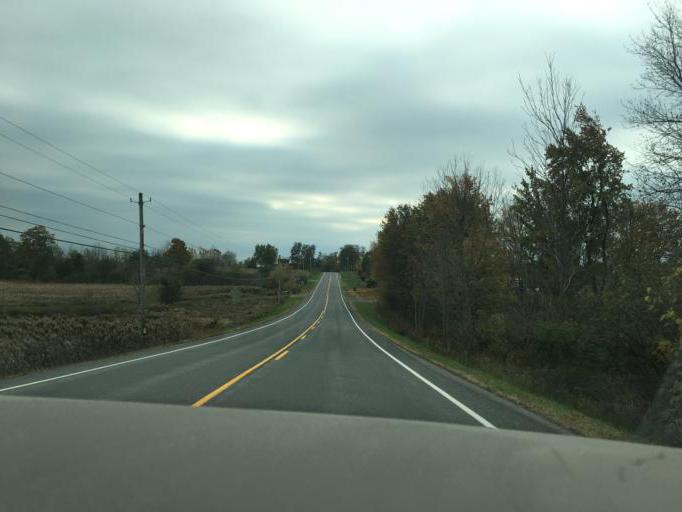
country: US
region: New York
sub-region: Wayne County
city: Macedon
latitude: 42.9985
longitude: -77.3255
